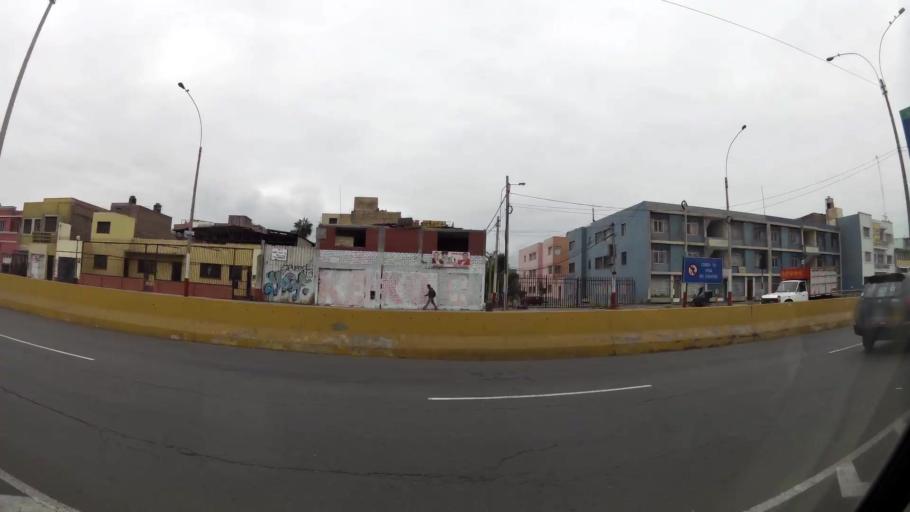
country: PE
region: Callao
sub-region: Callao
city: Callao
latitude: -12.0574
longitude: -77.1307
